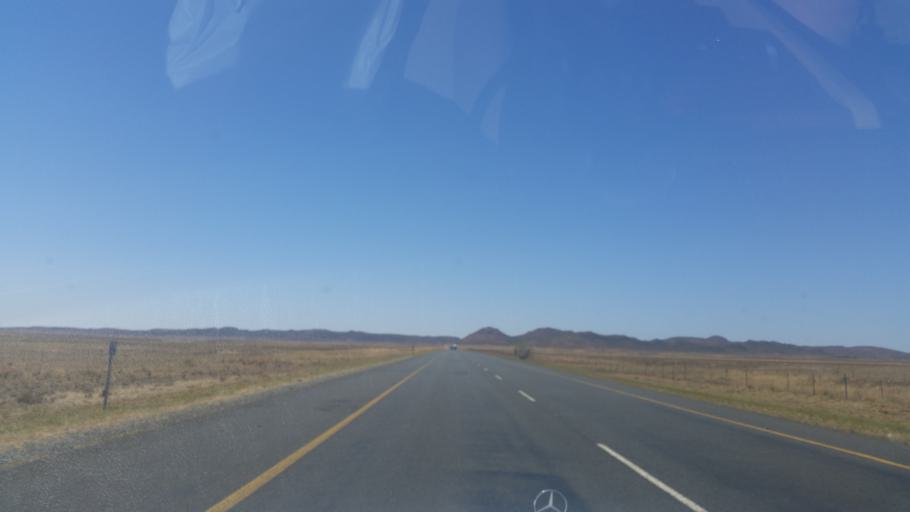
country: ZA
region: Northern Cape
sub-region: Pixley ka Seme District Municipality
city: Colesberg
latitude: -30.6821
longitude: 25.1605
